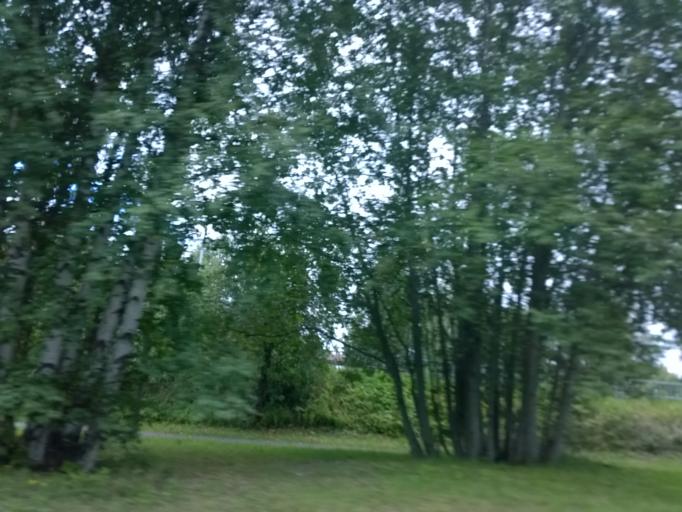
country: FI
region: Pirkanmaa
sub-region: Tampere
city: Tampere
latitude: 61.4872
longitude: 23.8225
